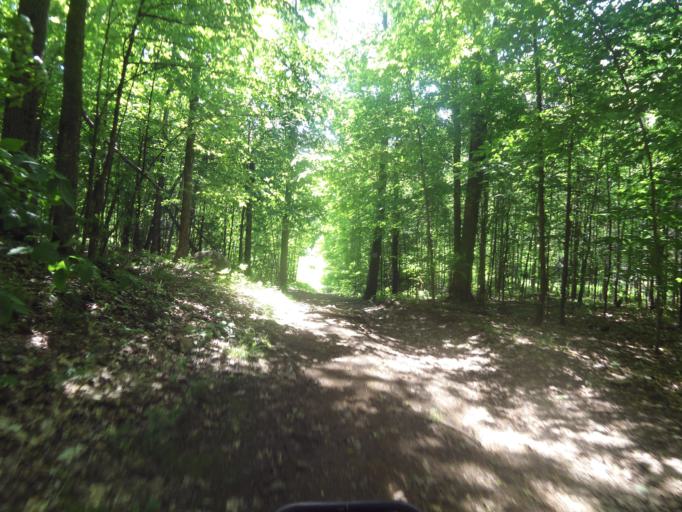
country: CA
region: Quebec
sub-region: Outaouais
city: Wakefield
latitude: 45.5409
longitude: -75.8888
